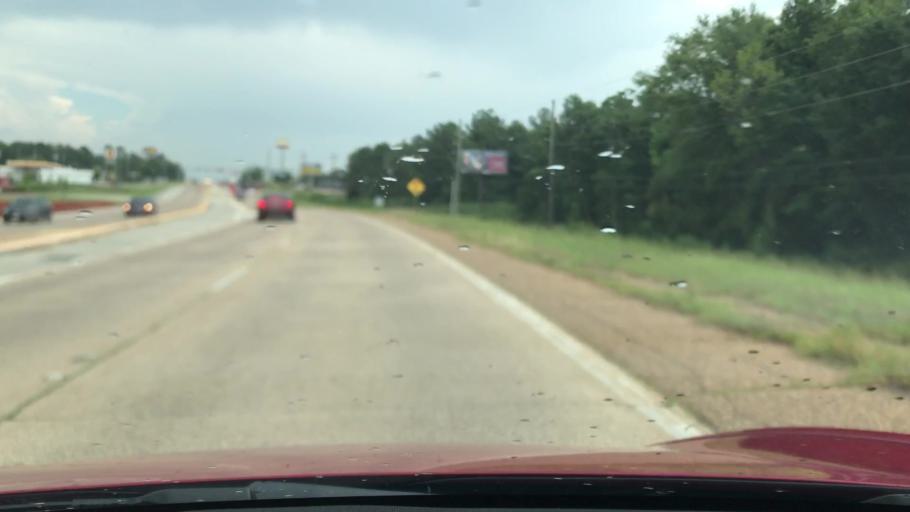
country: US
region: Louisiana
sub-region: Bossier Parish
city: Bossier City
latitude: 32.3982
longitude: -93.7674
